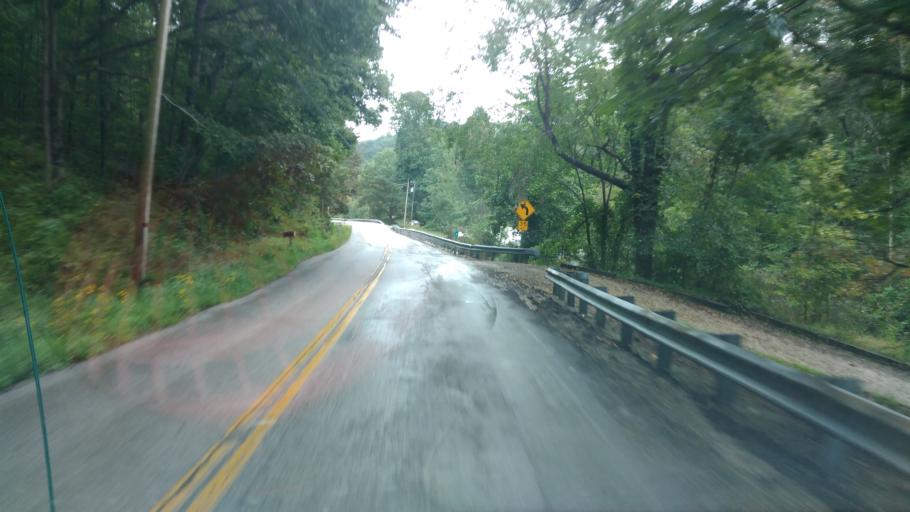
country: US
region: Kentucky
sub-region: Fleming County
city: Flemingsburg
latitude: 38.4512
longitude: -83.5199
